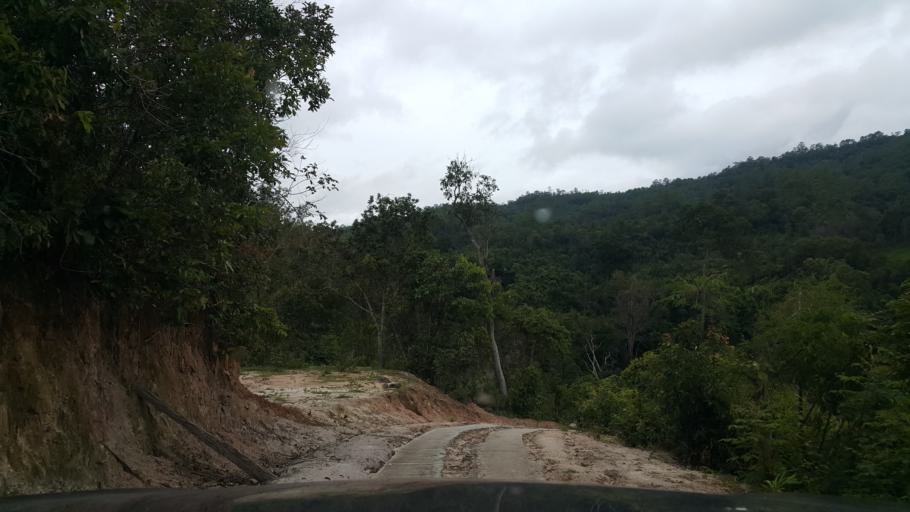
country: TH
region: Chiang Mai
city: Samoeng
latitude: 18.8100
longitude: 98.6247
